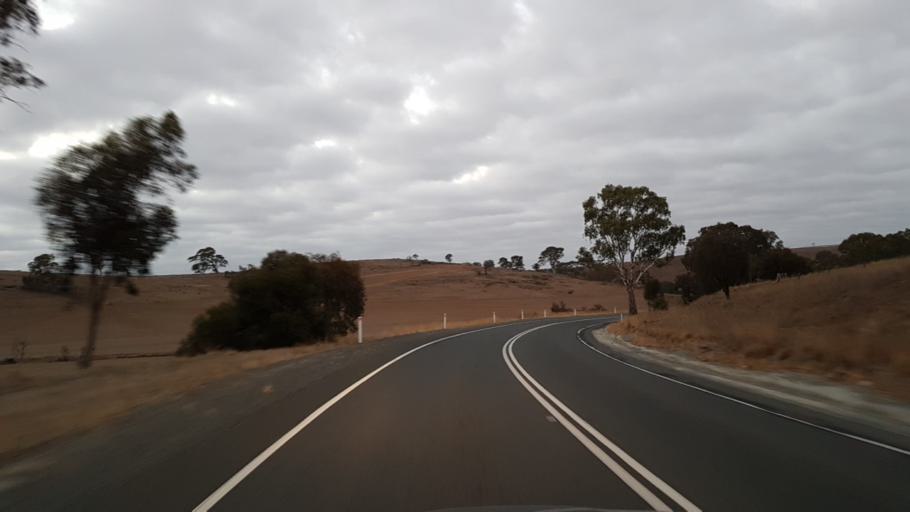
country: AU
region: South Australia
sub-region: Mount Barker
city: Nairne
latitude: -35.0364
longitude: 138.9862
